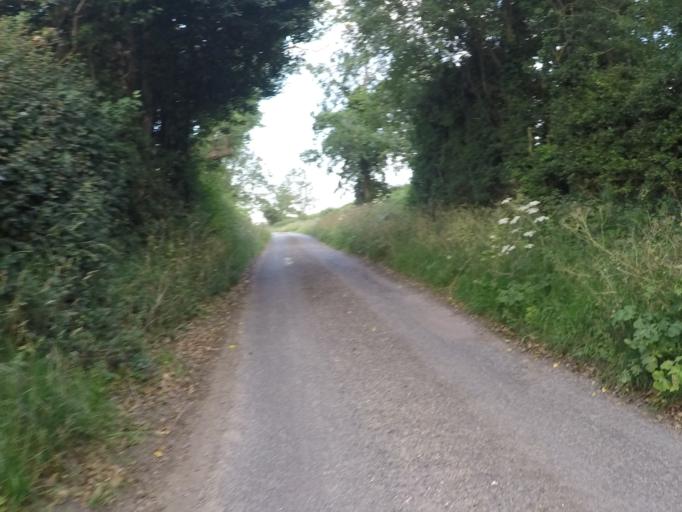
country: GB
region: England
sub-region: Oxfordshire
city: Charlbury
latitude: 51.8936
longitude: -1.4761
